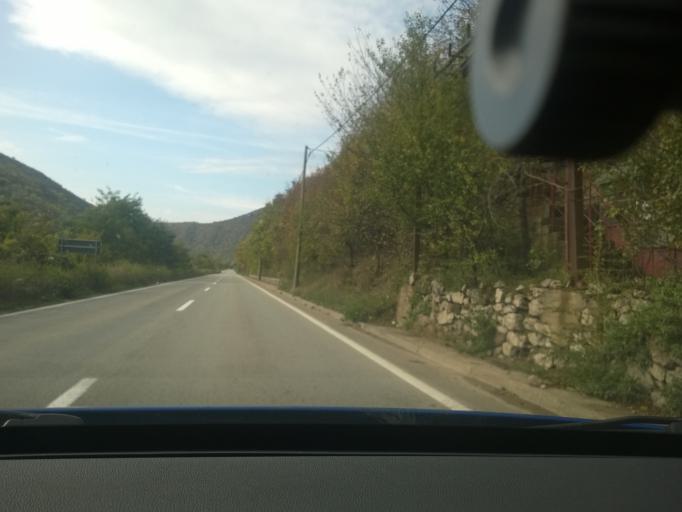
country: RS
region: Central Serbia
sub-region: Nisavski Okrug
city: Niska Banja
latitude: 43.3299
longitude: 22.0635
